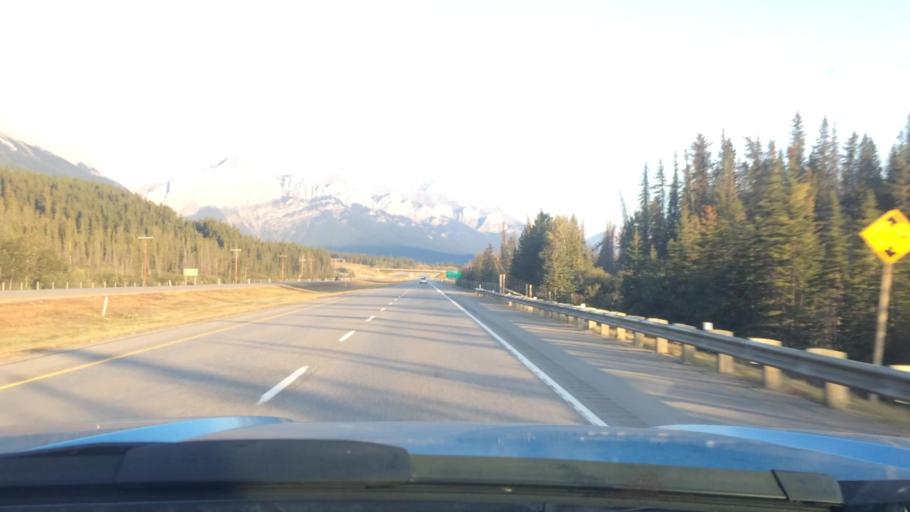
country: CA
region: Alberta
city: Canmore
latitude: 51.0498
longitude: -115.3004
